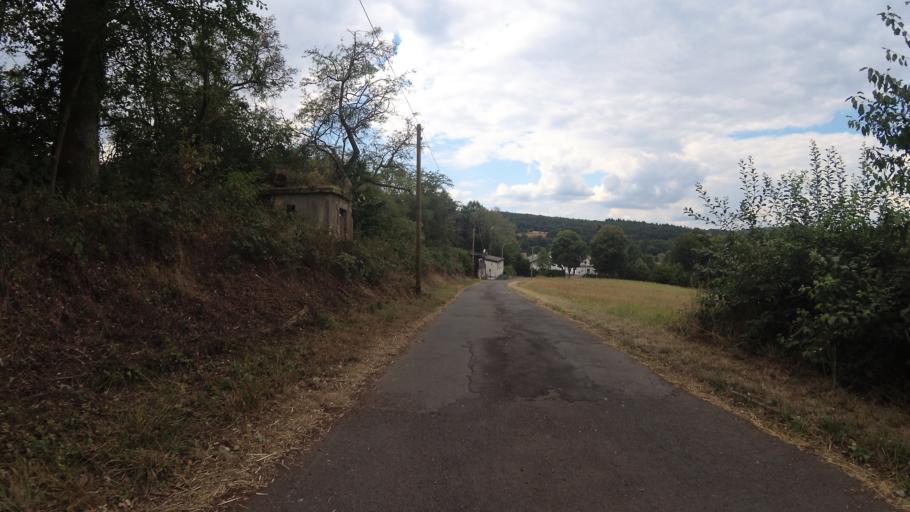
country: DE
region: Rheinland-Pfalz
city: Breitenbach
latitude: 49.4337
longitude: 7.2394
